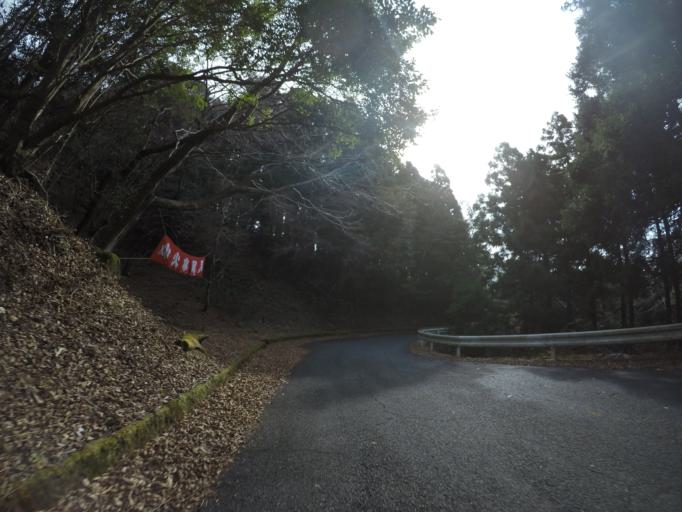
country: JP
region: Shizuoka
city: Heda
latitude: 34.8475
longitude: 138.8508
